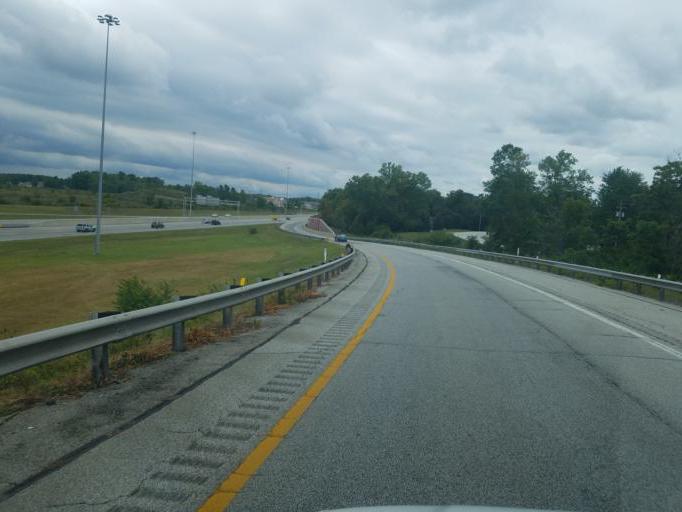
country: US
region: Ohio
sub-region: Lake County
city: Fairport Harbor
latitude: 41.7224
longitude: -81.2846
